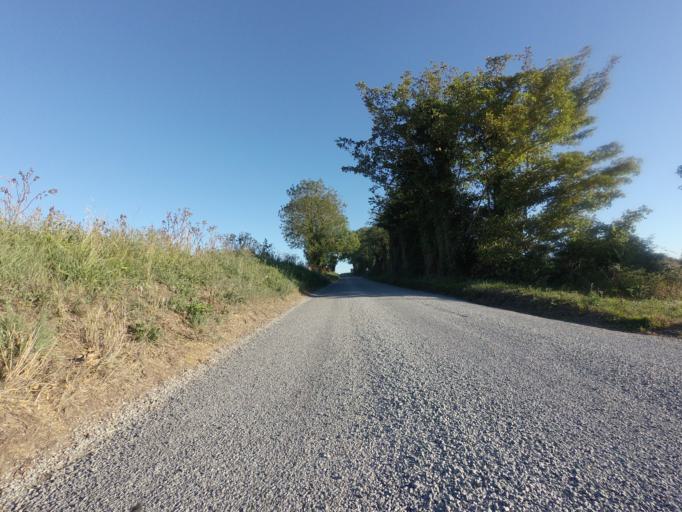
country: GB
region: England
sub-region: Kent
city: Herne Bay
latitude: 51.3419
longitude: 1.1898
